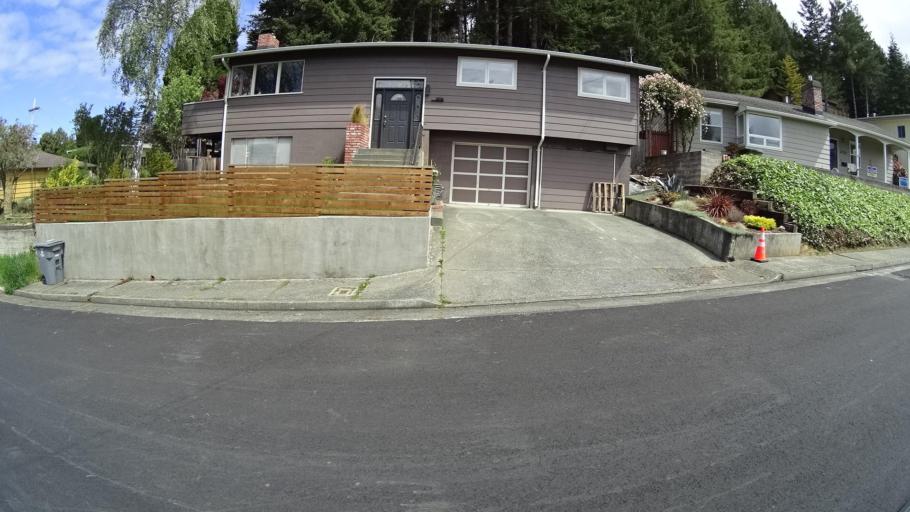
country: US
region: California
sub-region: Humboldt County
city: Bayside
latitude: 40.8581
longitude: -124.0598
